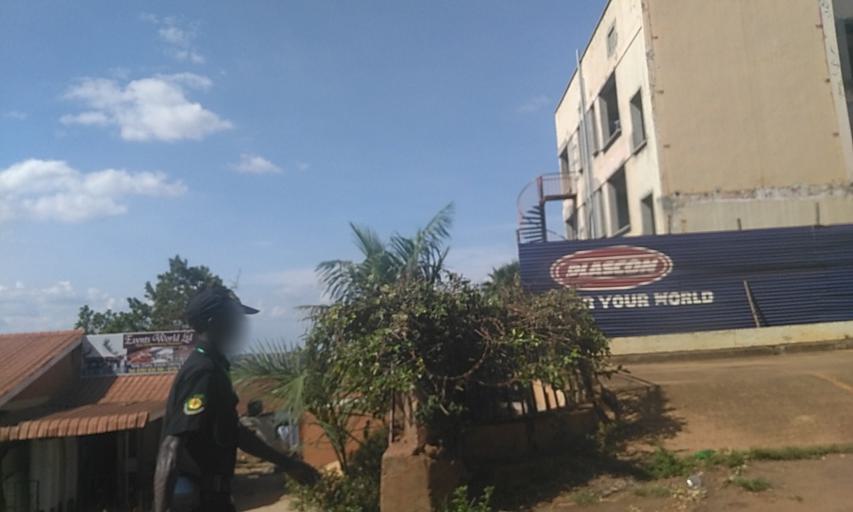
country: UG
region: Central Region
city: Kampala Central Division
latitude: 0.3499
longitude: 32.6028
